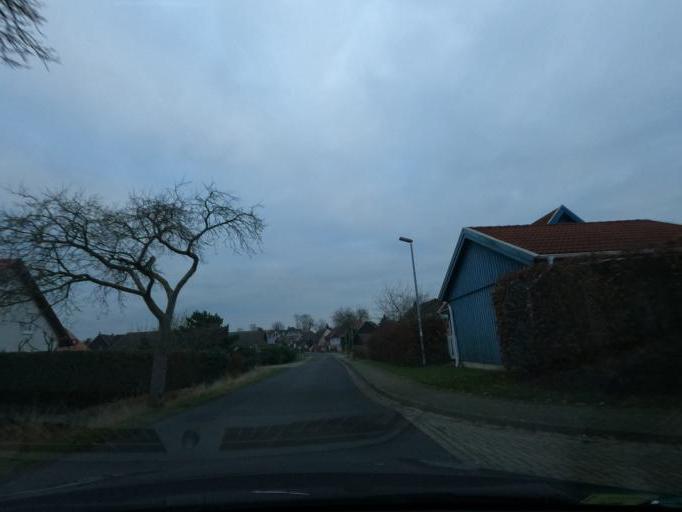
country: DE
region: Lower Saxony
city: Wittmar
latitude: 52.1239
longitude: 10.6153
